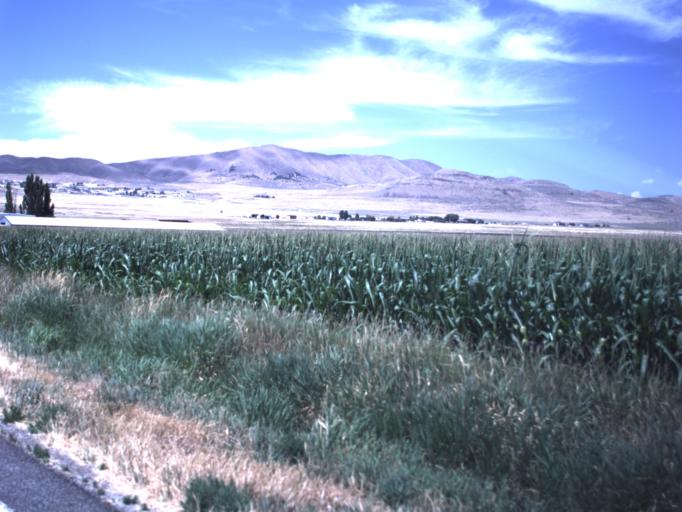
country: US
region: Utah
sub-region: Box Elder County
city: Tremonton
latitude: 41.6946
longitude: -112.2846
